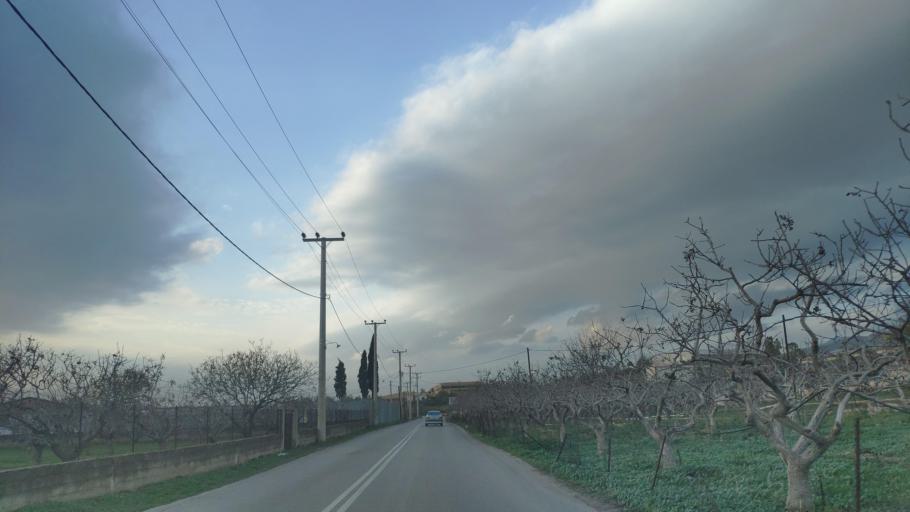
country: GR
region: Attica
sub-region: Nomarchia Dytikis Attikis
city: Nea Peramos
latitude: 37.9942
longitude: 23.3961
